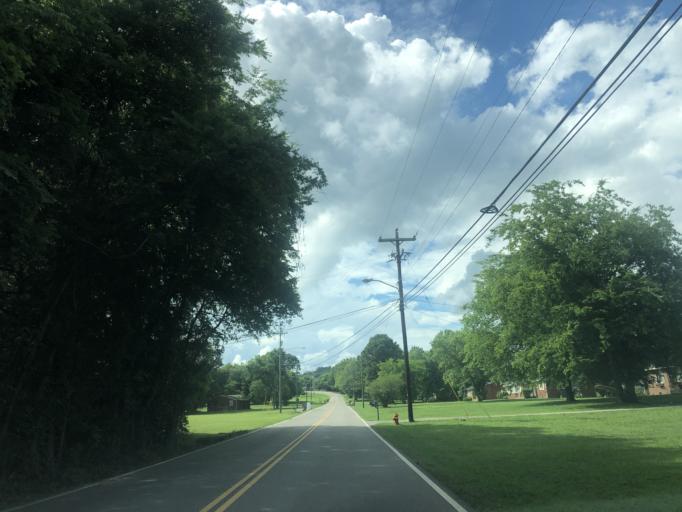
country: US
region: Tennessee
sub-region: Davidson County
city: Nashville
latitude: 36.2160
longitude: -86.8679
